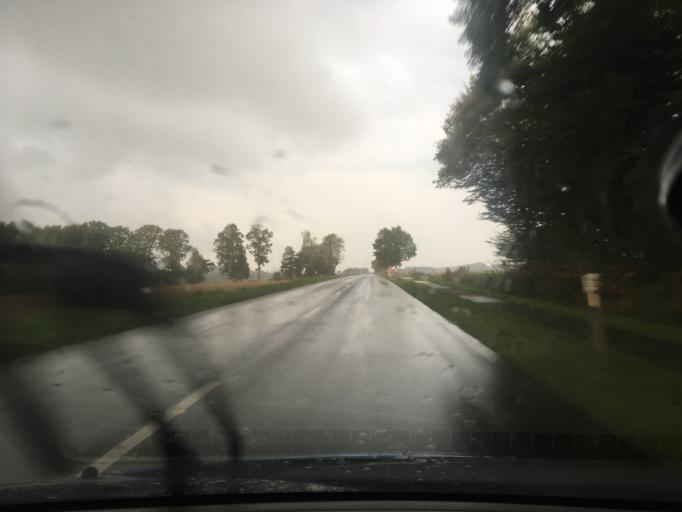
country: DE
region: Lower Saxony
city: Soderstorf
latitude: 53.1540
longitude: 10.1548
